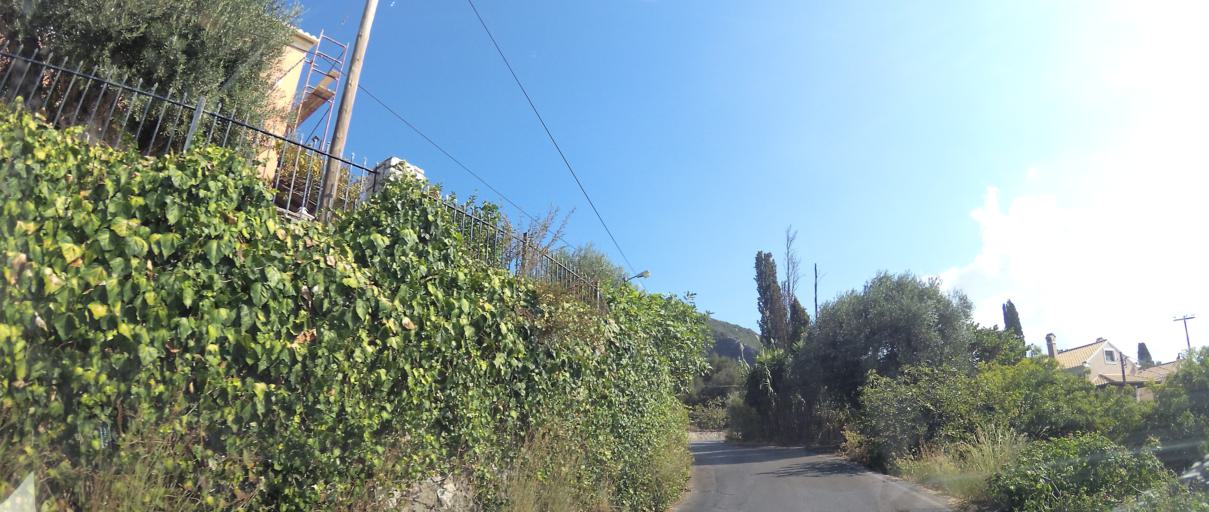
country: GR
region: Ionian Islands
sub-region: Nomos Kerkyras
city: Kontokali
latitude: 39.7195
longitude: 19.8449
